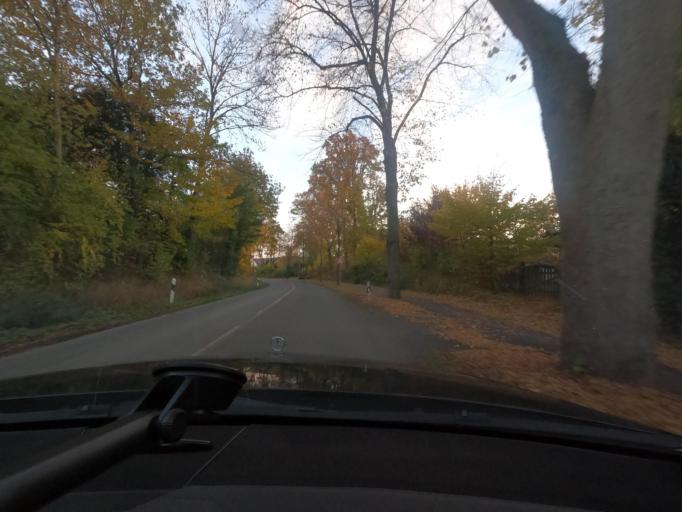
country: DE
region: North Rhine-Westphalia
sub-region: Regierungsbezirk Arnsberg
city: Mohnesee
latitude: 51.4928
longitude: 8.1356
